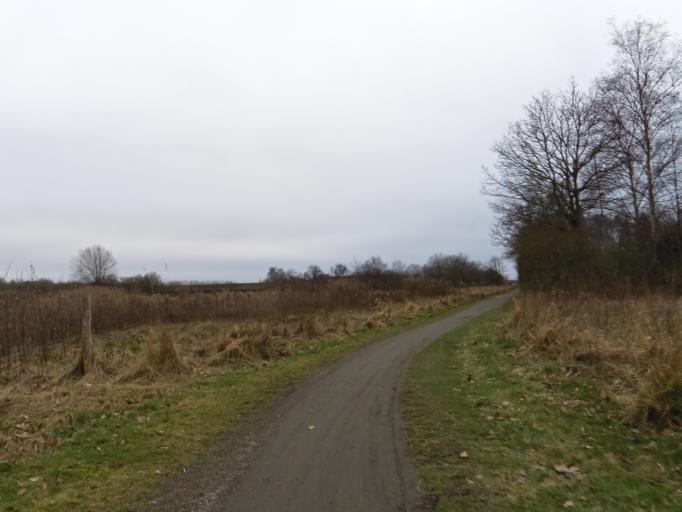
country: DK
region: South Denmark
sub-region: Odense Kommune
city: Neder Holluf
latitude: 55.3817
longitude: 10.4401
